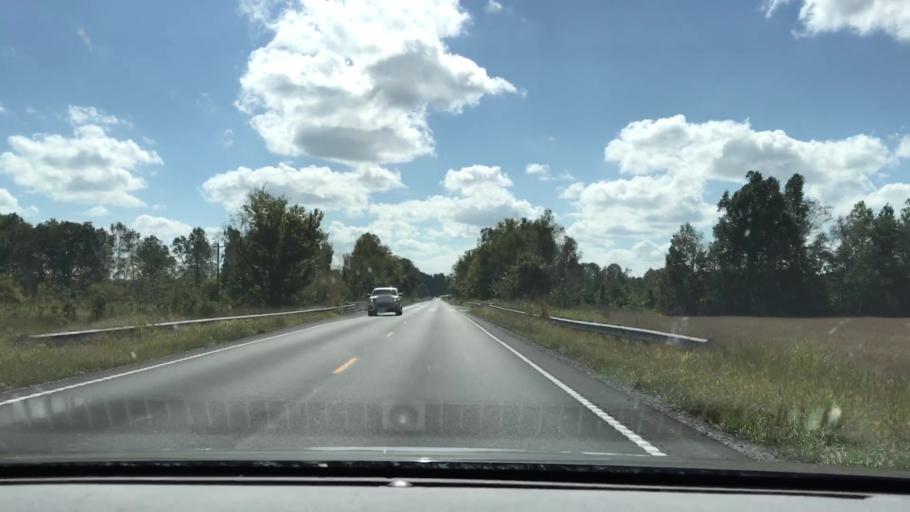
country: US
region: Kentucky
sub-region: Graves County
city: Mayfield
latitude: 36.8646
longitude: -88.5731
